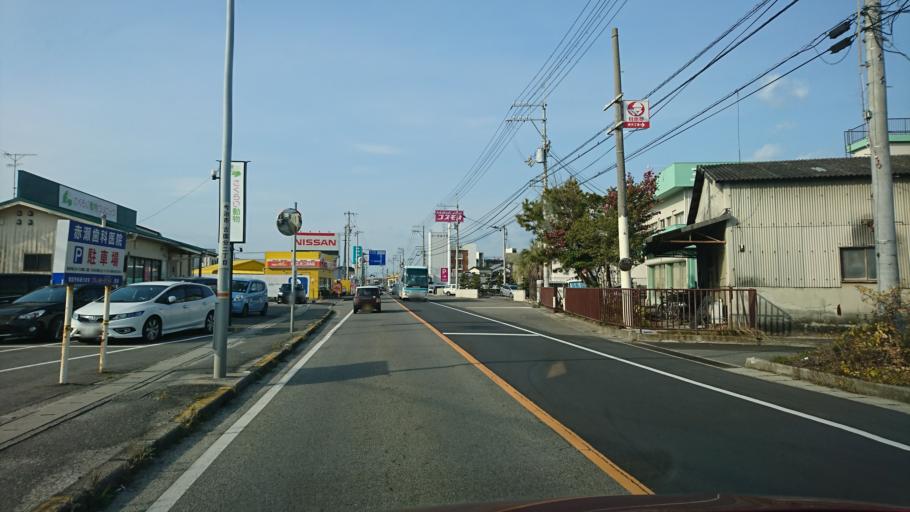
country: JP
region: Ehime
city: Saijo
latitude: 34.0348
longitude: 133.0344
